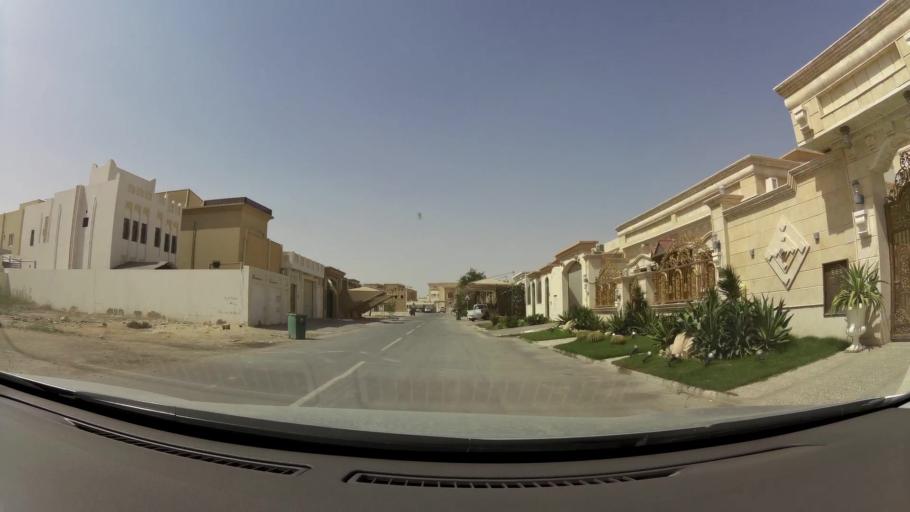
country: QA
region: Baladiyat Umm Salal
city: Umm Salal Muhammad
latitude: 25.3907
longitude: 51.4184
